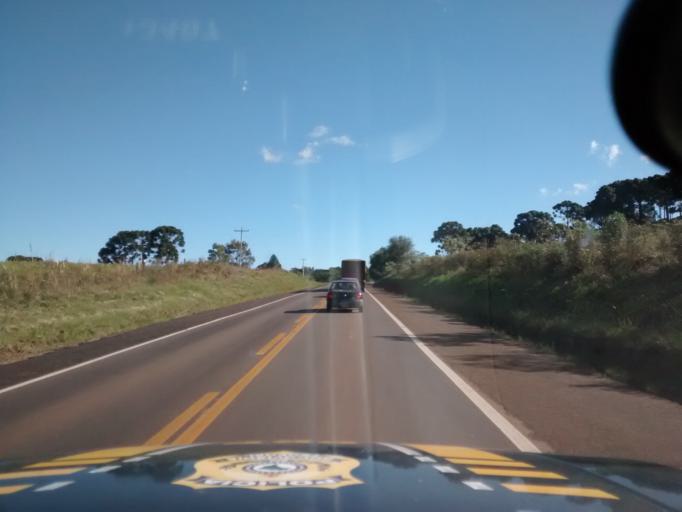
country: BR
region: Rio Grande do Sul
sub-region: Lagoa Vermelha
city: Lagoa Vermelha
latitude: -28.2972
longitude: -51.4491
